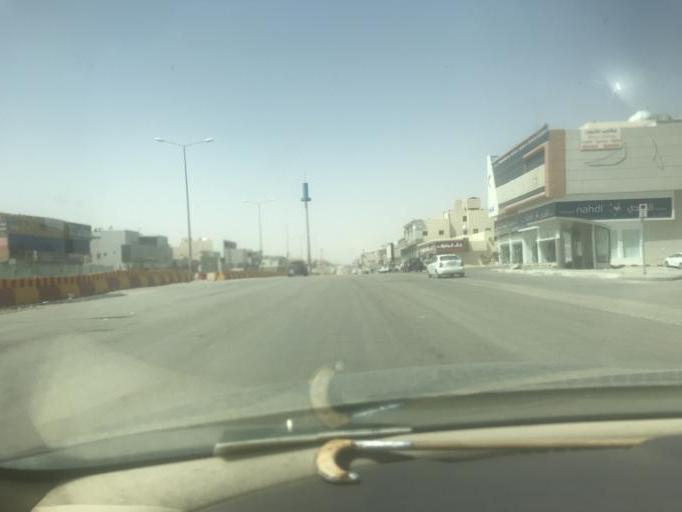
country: SA
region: Ar Riyad
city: Riyadh
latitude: 24.8112
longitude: 46.6002
